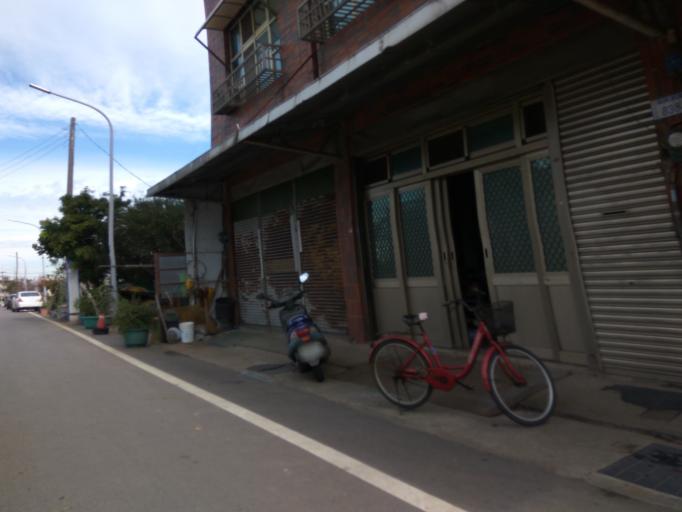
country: TW
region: Taiwan
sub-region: Hsinchu
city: Zhubei
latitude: 24.9850
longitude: 121.1058
